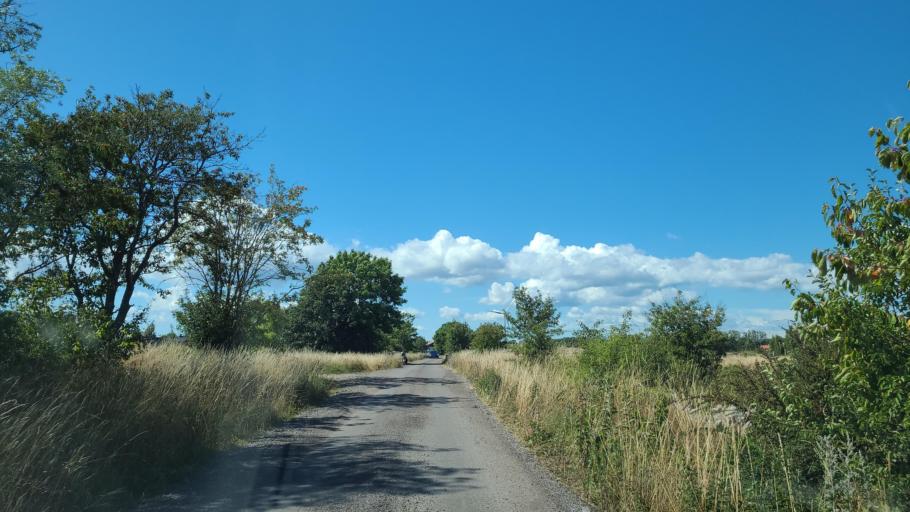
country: SE
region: Kalmar
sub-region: Morbylanga Kommun
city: Sodra Sandby
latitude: 56.7130
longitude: 16.7113
